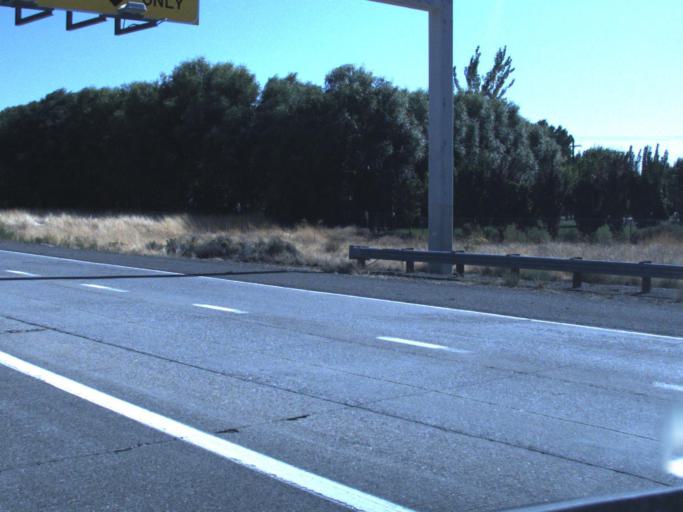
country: US
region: Washington
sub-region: Franklin County
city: Pasco
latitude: 46.2501
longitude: -119.1327
